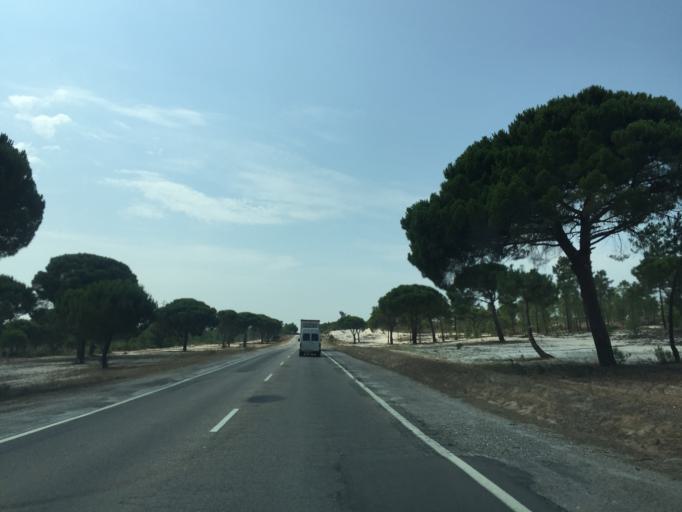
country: PT
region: Setubal
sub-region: Grandola
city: Grandola
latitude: 38.2604
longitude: -8.5449
